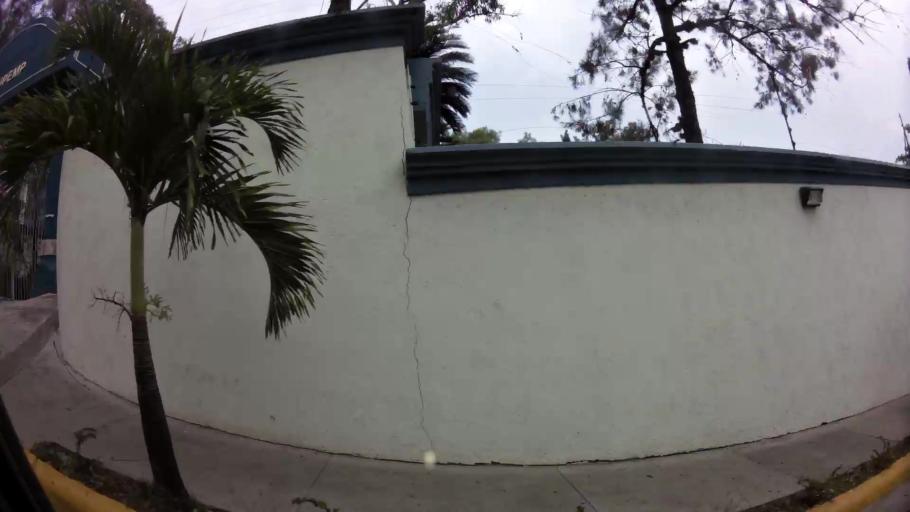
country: HN
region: Francisco Morazan
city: Tegucigalpa
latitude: 14.0834
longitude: -87.1889
